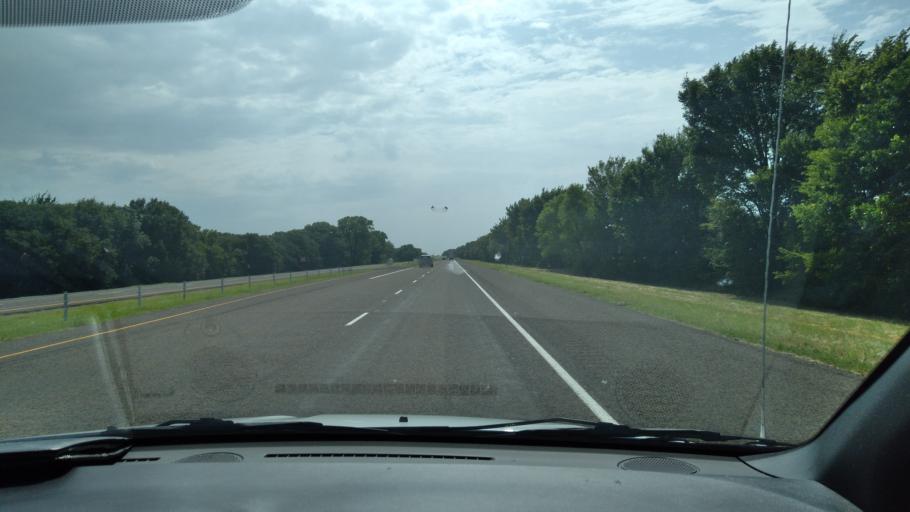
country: US
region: Texas
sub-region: Navarro County
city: Kerens
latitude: 32.1257
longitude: -96.2743
